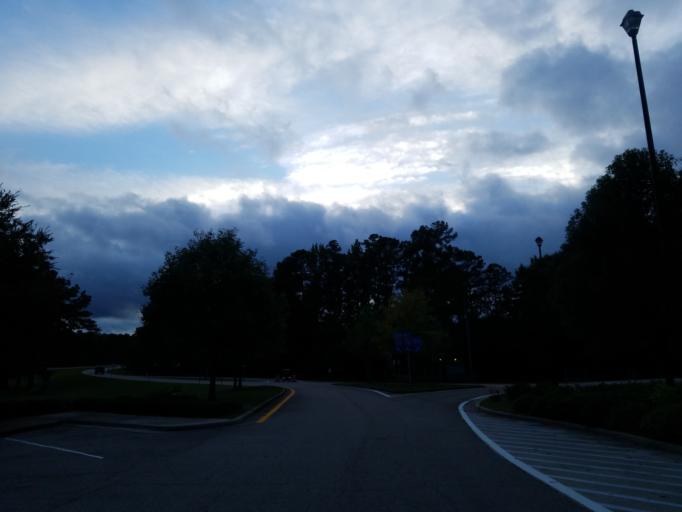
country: US
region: Mississippi
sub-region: Lauderdale County
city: Marion
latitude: 32.4109
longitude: -88.5352
